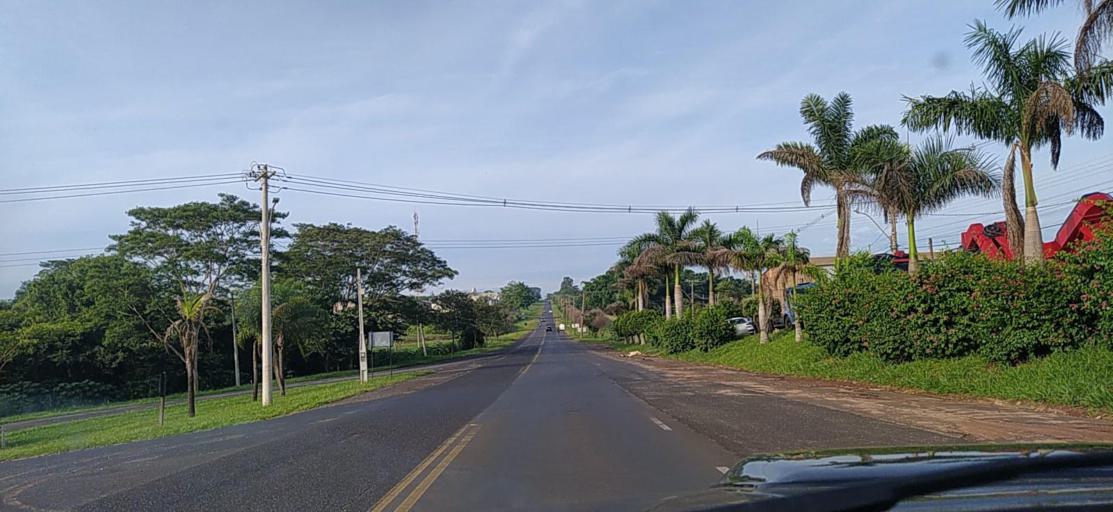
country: BR
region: Sao Paulo
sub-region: Pindorama
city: Pindorama
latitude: -21.1924
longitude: -48.9139
